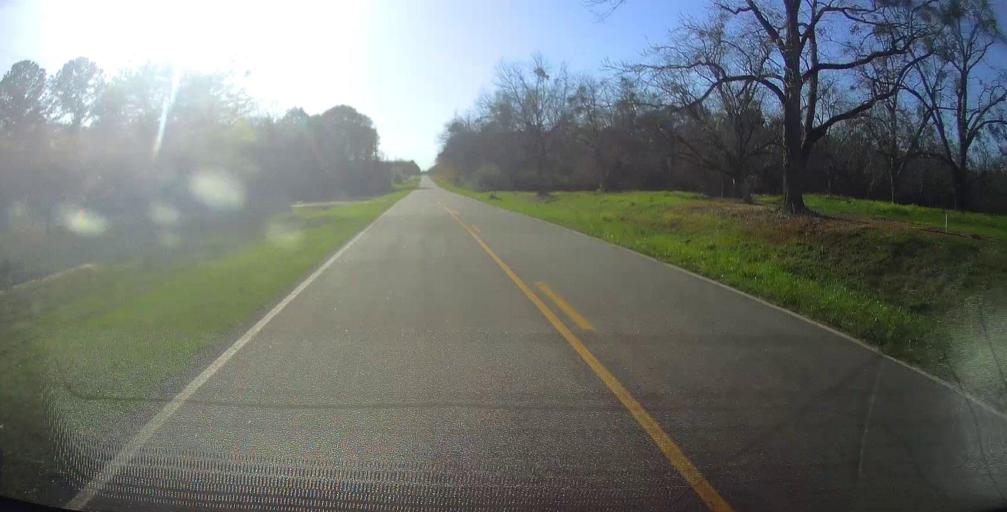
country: US
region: Georgia
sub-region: Pulaski County
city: Hawkinsville
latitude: 32.3473
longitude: -83.5792
